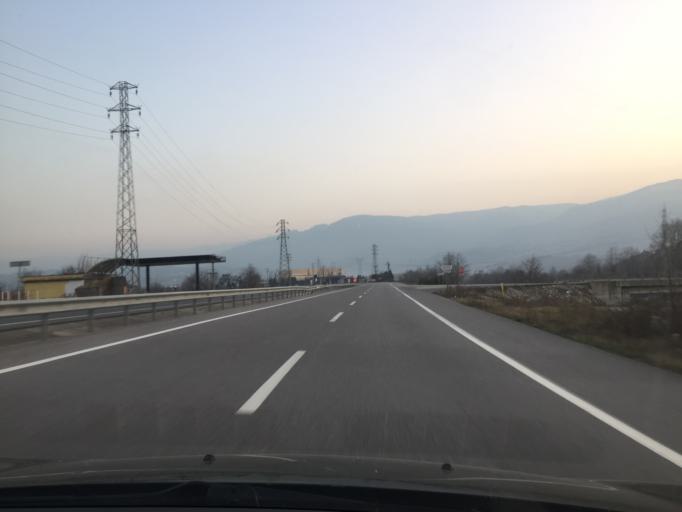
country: TR
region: Sakarya
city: Akyazi
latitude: 40.6443
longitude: 30.6126
